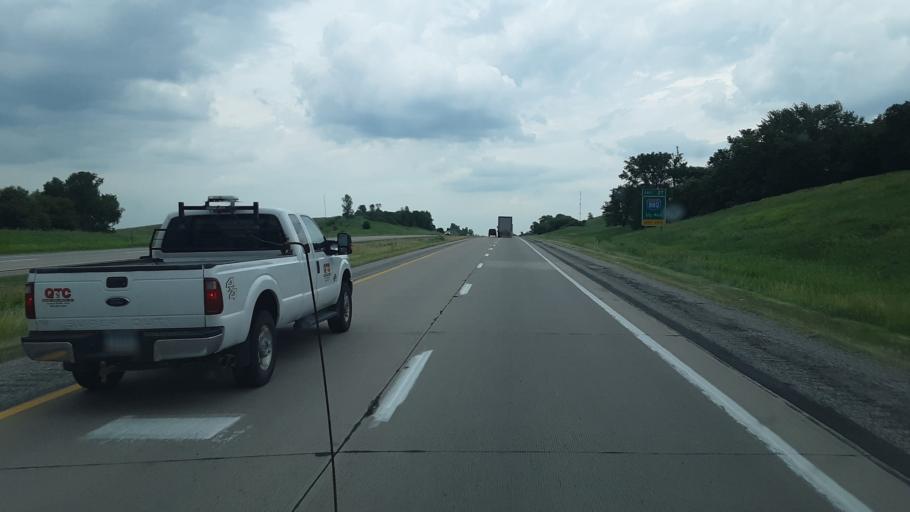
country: US
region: Iowa
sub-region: Pottawattamie County
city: Avoca
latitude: 41.4802
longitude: -95.5885
